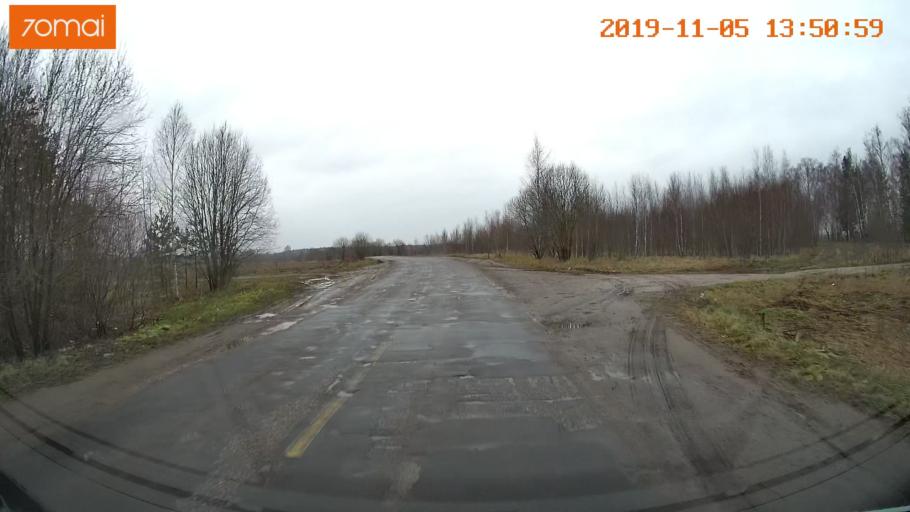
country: RU
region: Ivanovo
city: Kaminskiy
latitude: 57.0230
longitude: 41.4050
